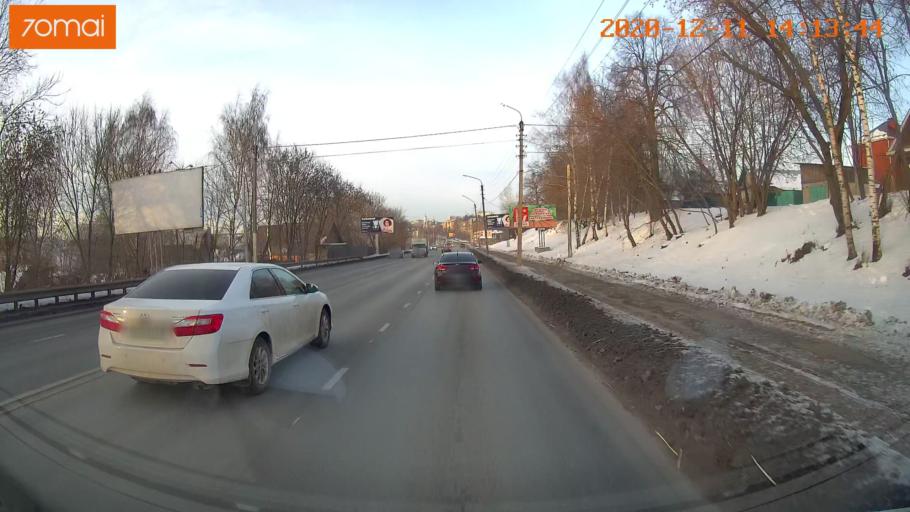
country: RU
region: Kostroma
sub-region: Kostromskoy Rayon
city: Kostroma
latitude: 57.7477
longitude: 40.9564
